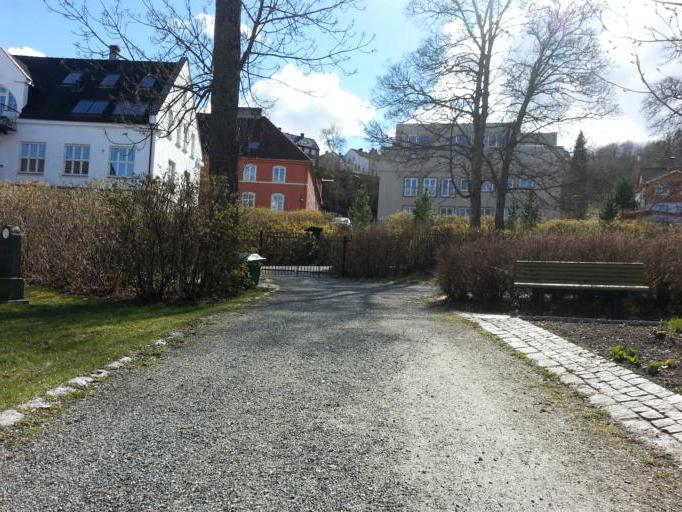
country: NO
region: Sor-Trondelag
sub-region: Trondheim
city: Trondheim
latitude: 63.4305
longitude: 10.3577
